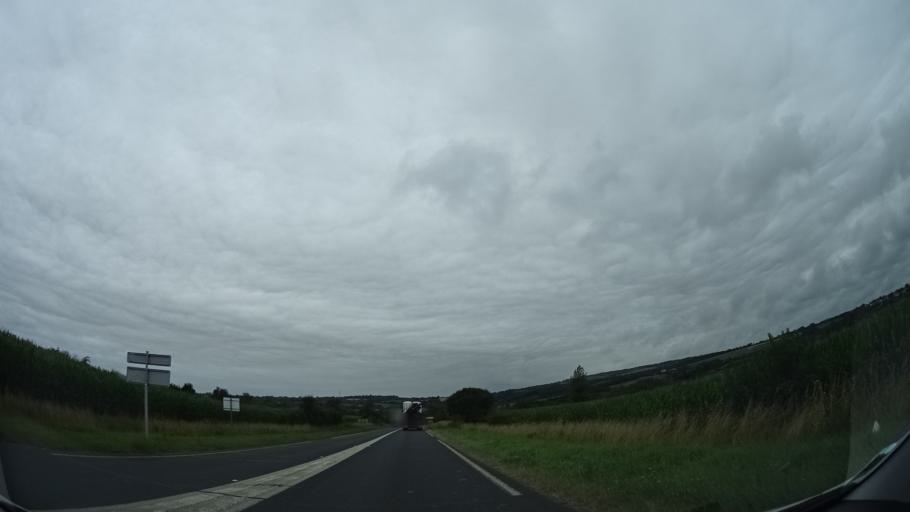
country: FR
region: Lower Normandy
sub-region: Departement de la Manche
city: Barneville-Plage
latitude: 49.3794
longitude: -1.7432
